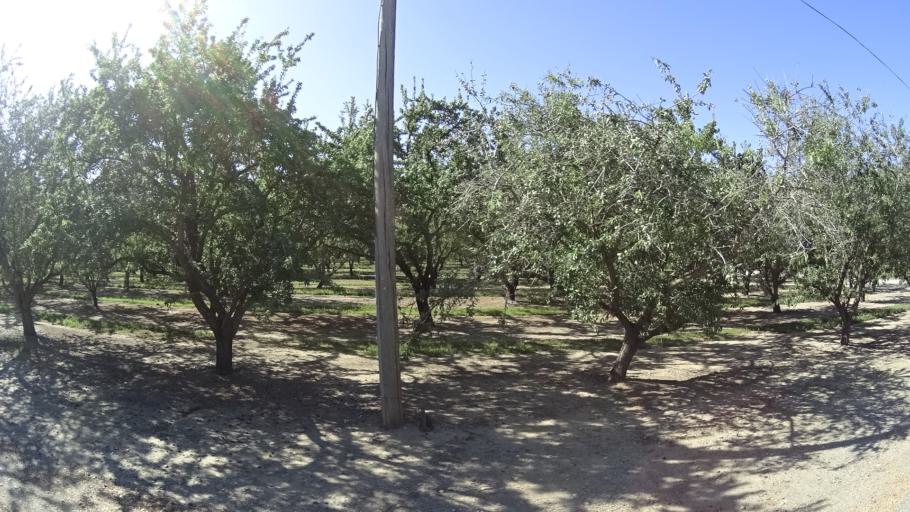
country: US
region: California
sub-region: Glenn County
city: Hamilton City
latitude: 39.7129
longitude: -121.9970
